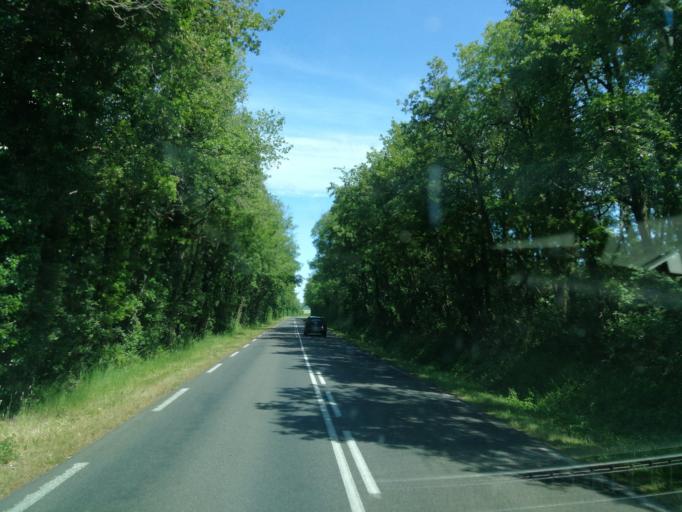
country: FR
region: Poitou-Charentes
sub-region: Departement des Deux-Sevres
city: Saint-Leger-de-Montbrun
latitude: 46.9716
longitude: -0.1653
